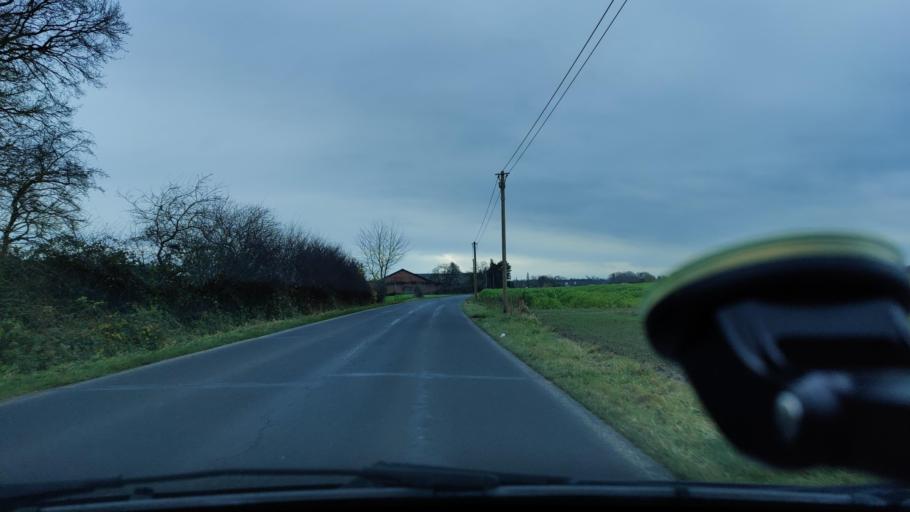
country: DE
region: North Rhine-Westphalia
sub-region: Regierungsbezirk Dusseldorf
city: Alpen
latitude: 51.6038
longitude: 6.4776
